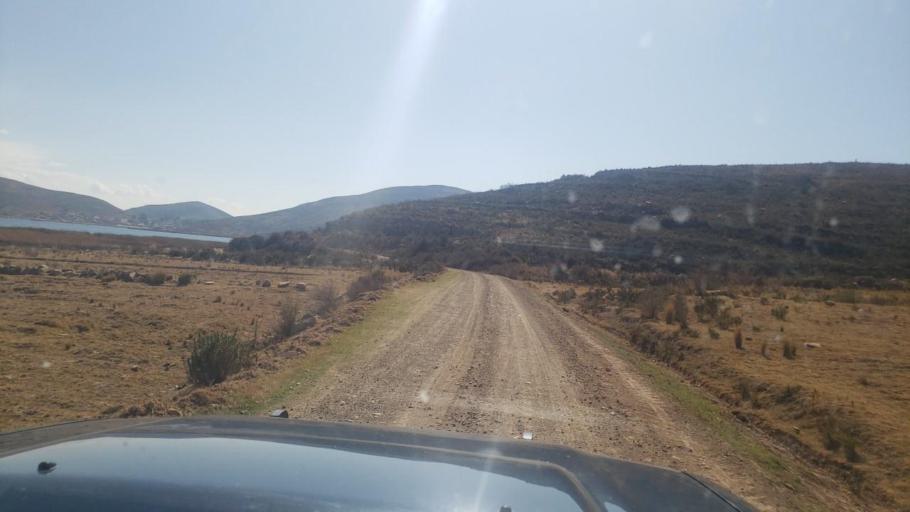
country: BO
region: La Paz
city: Huatajata
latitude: -16.3357
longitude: -68.6904
